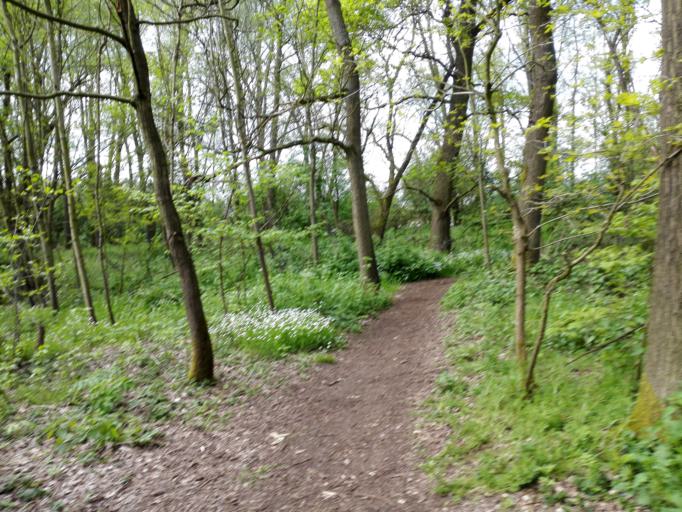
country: BE
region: Flanders
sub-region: Provincie Vlaams-Brabant
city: Rotselaar
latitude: 50.9579
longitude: 4.7310
